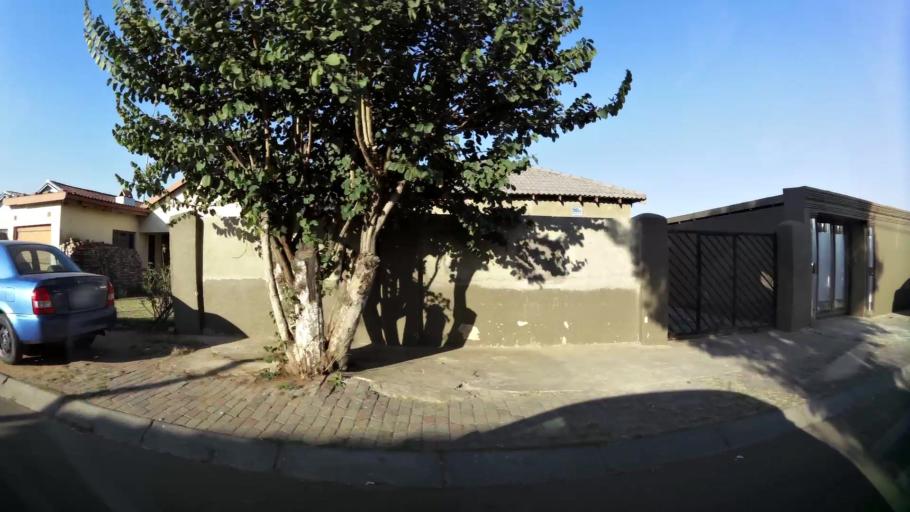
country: ZA
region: Gauteng
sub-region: City of Johannesburg Metropolitan Municipality
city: Soweto
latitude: -26.2601
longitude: 27.8844
